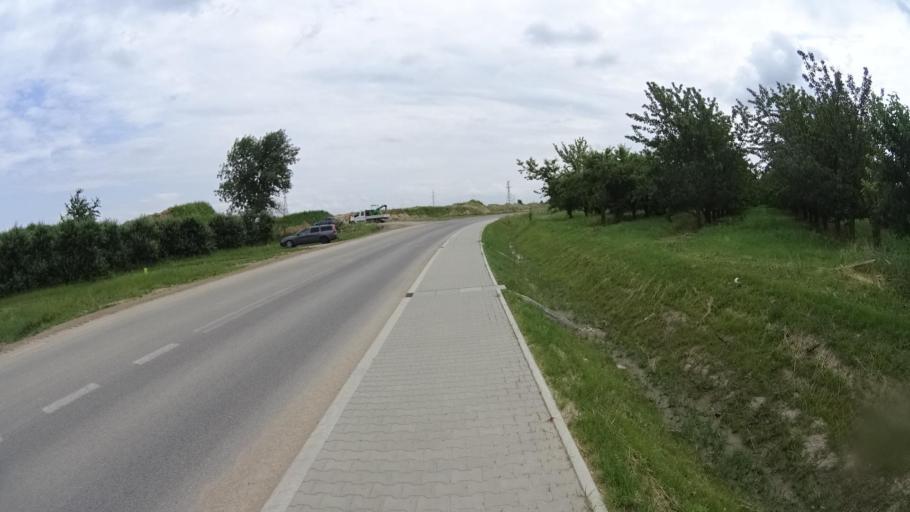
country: PL
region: Masovian Voivodeship
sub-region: Powiat piaseczynski
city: Tarczyn
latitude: 51.9514
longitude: 20.8408
